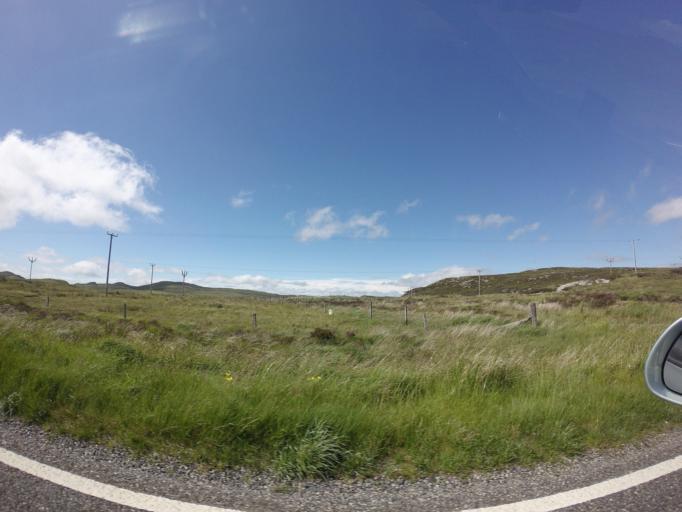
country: GB
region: Scotland
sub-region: Eilean Siar
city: Stornoway
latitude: 58.1192
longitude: -6.5123
